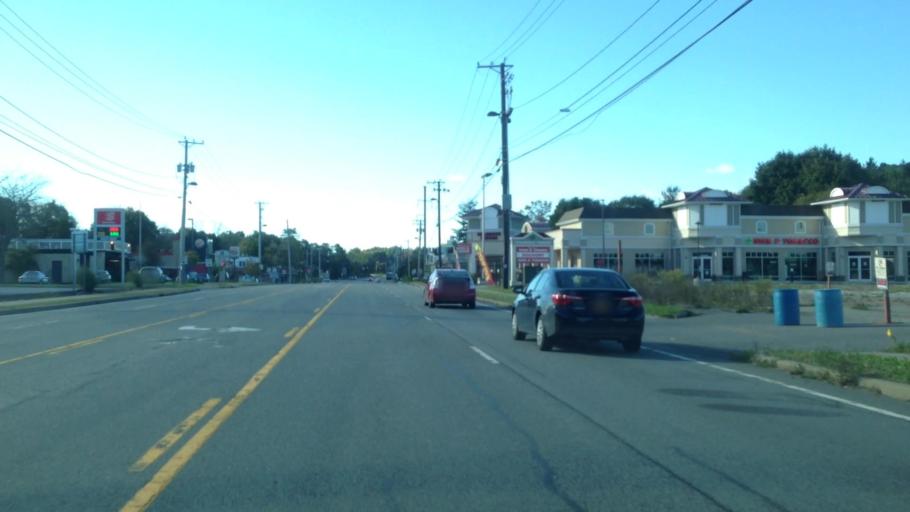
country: US
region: New York
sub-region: Ulster County
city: Highland
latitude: 41.7150
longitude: -73.9635
